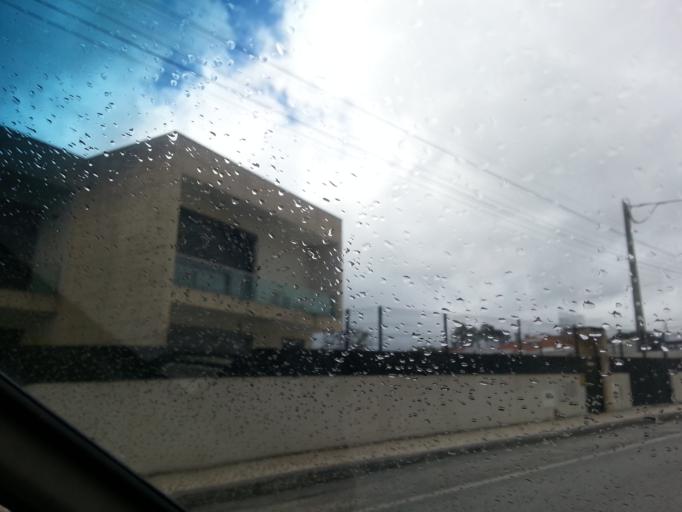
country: PT
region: Viseu
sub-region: Viseu
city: Rio de Loba
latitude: 40.6361
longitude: -7.8665
